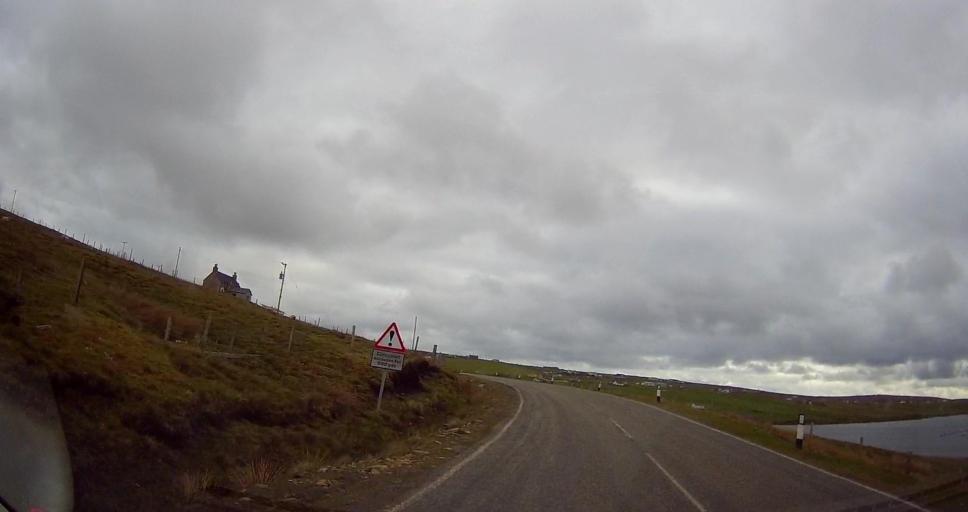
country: GB
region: Scotland
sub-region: Shetland Islands
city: Shetland
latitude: 60.6087
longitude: -1.0777
